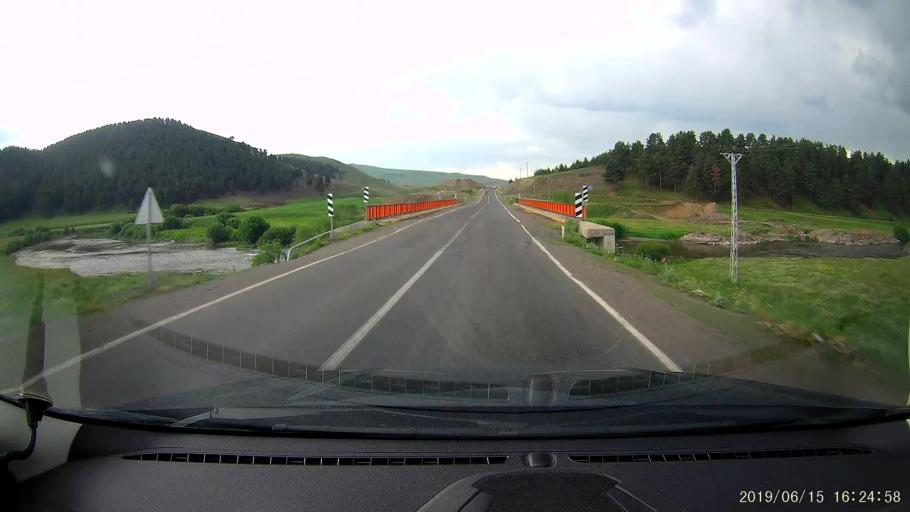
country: TR
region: Ardahan
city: Hanak
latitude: 41.1602
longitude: 42.8719
